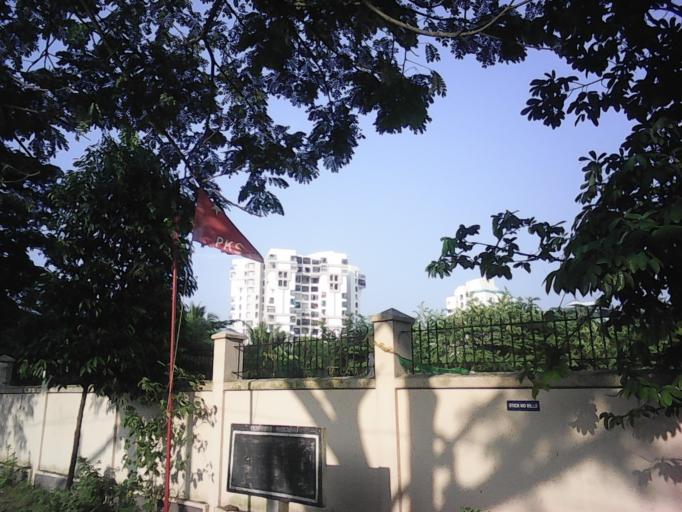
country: IN
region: Kerala
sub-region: Ernakulam
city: Cochin
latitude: 9.9526
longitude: 76.2949
